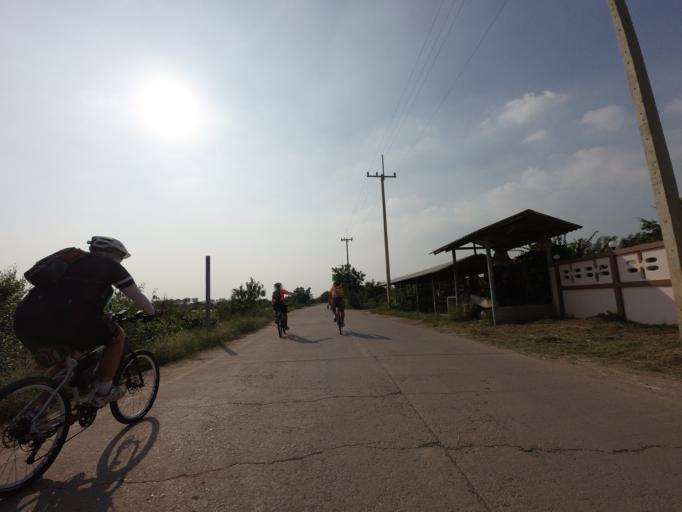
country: TH
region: Samut Sakhon
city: Samut Sakhon
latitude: 13.4986
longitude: 100.3436
